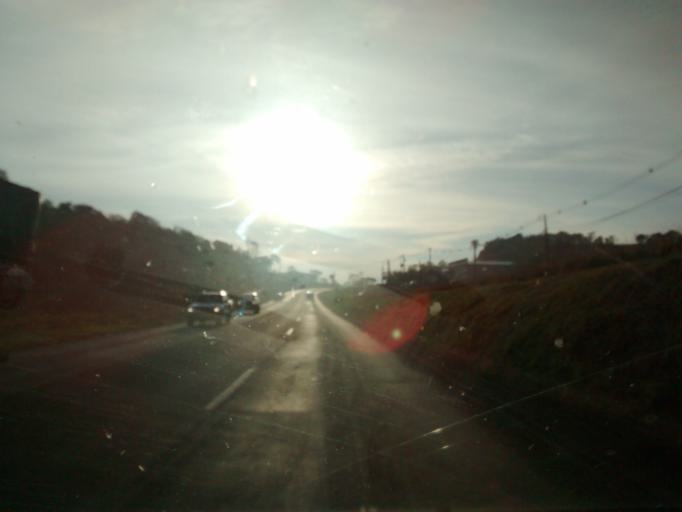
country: BR
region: Parana
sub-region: Francisco Beltrao
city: Francisco Beltrao
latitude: -26.1468
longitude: -52.9994
